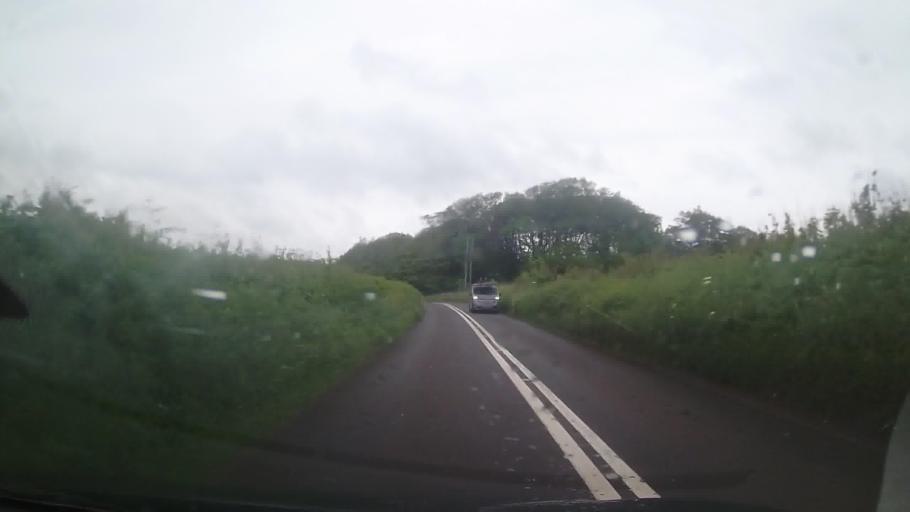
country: GB
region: England
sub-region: Borough of Torbay
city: Brixham
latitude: 50.3756
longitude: -3.5474
